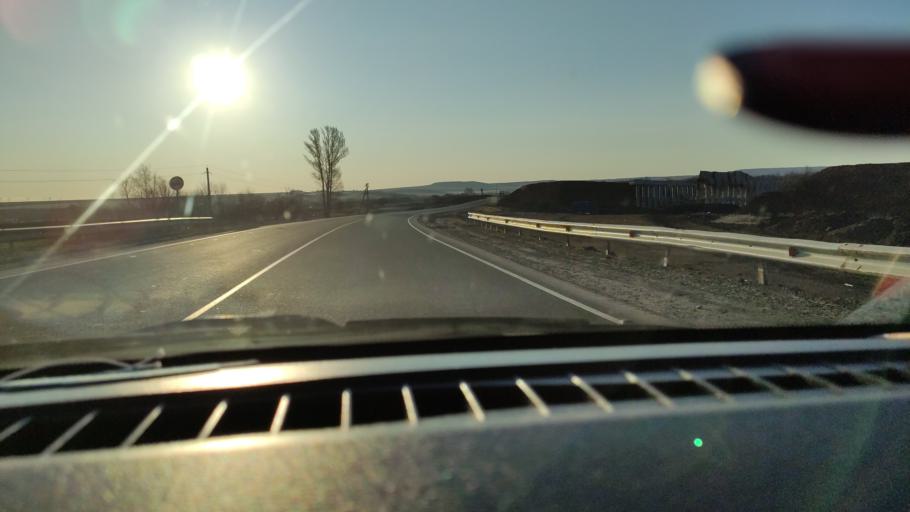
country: RU
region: Saratov
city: Sennoy
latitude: 52.1611
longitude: 47.0521
